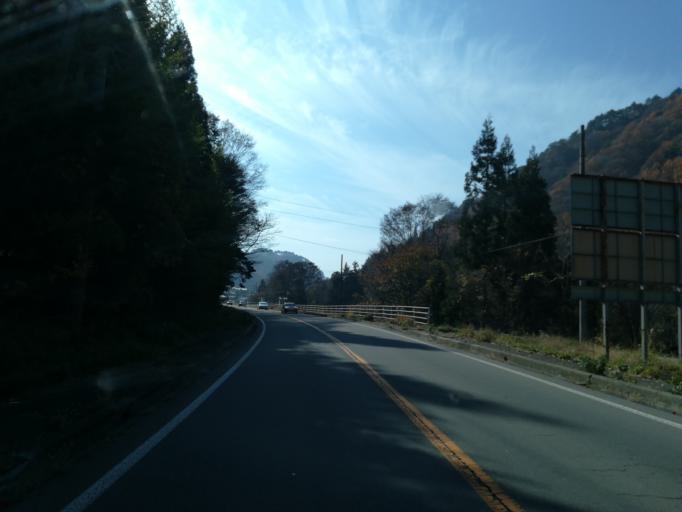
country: JP
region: Nagano
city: Ueda
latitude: 36.4552
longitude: 138.3325
